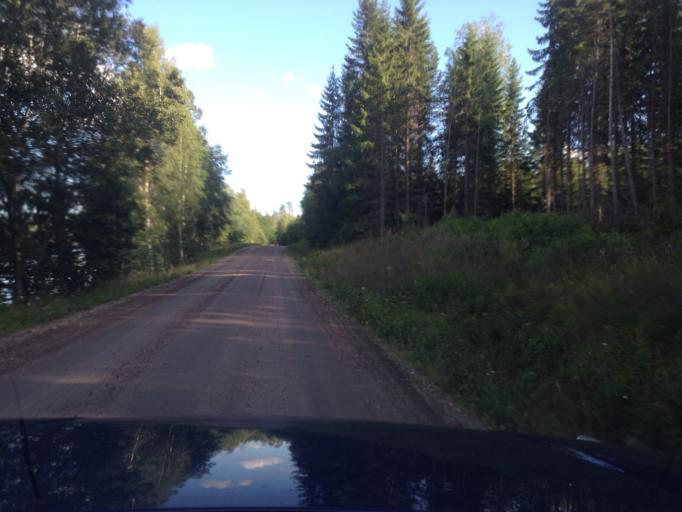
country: SE
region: Dalarna
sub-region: Ludvika Kommun
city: Abborrberget
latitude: 60.2851
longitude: 14.7194
